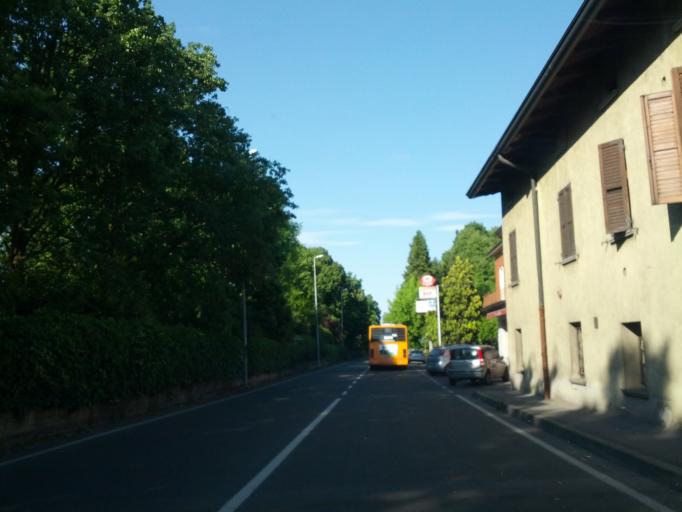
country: IT
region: Emilia-Romagna
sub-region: Provincia di Reggio Emilia
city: Reggio nell'Emilia
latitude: 44.6715
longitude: 10.6072
